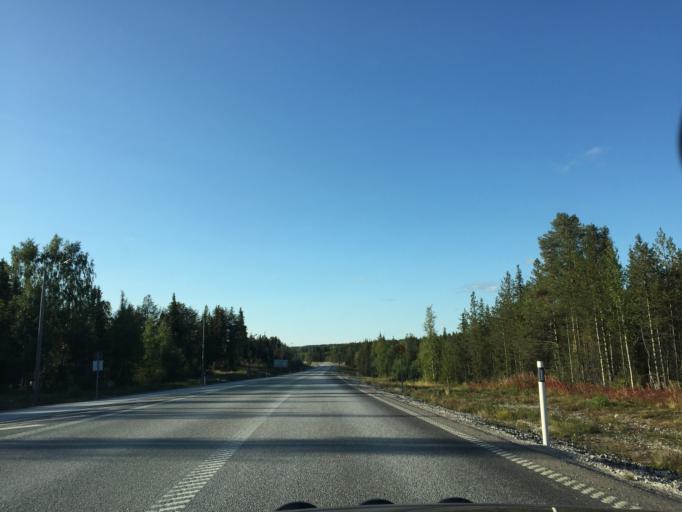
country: SE
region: Norrbotten
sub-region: Gallivare Kommun
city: Malmberget
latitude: 67.6362
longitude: 21.0664
